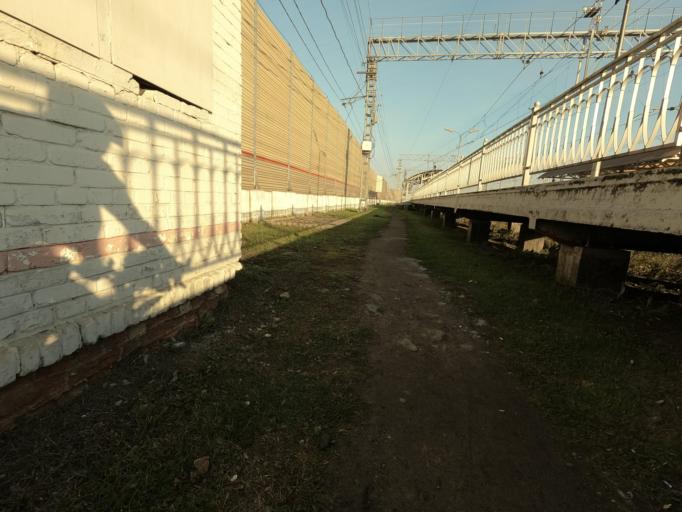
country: RU
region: Leningrad
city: Mga
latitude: 59.7557
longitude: 31.0629
